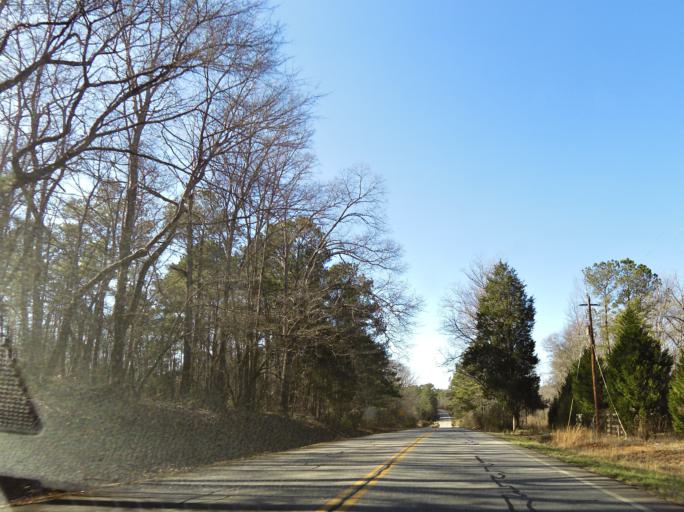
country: US
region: Georgia
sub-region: Lamar County
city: Barnesville
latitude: 32.9167
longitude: -84.1729
